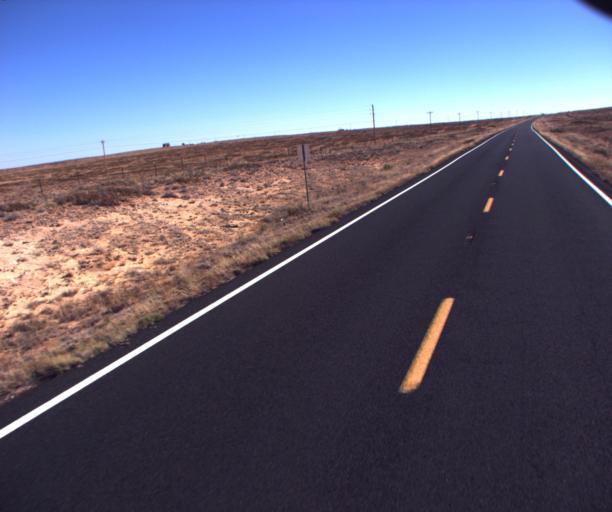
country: US
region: Arizona
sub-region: Coconino County
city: Tuba City
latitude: 36.0105
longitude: -111.0687
